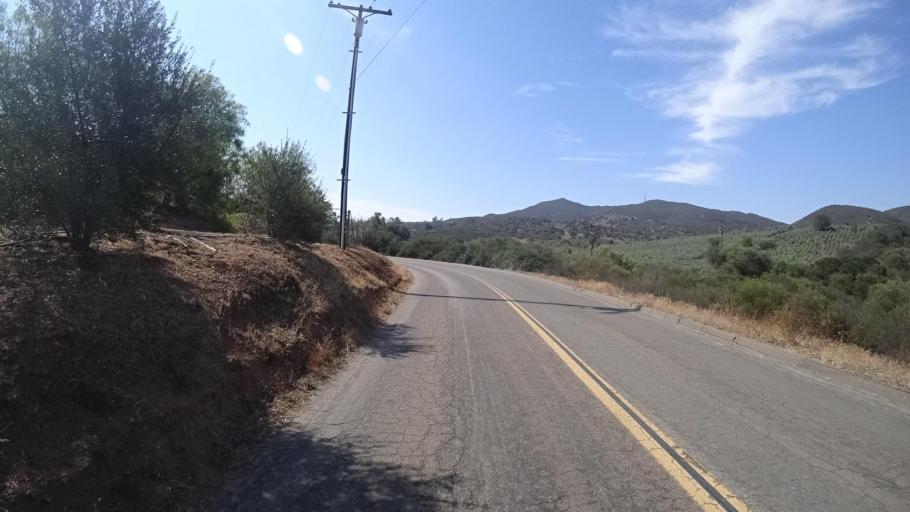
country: US
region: California
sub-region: San Diego County
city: Hidden Meadows
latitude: 33.2281
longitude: -117.1783
